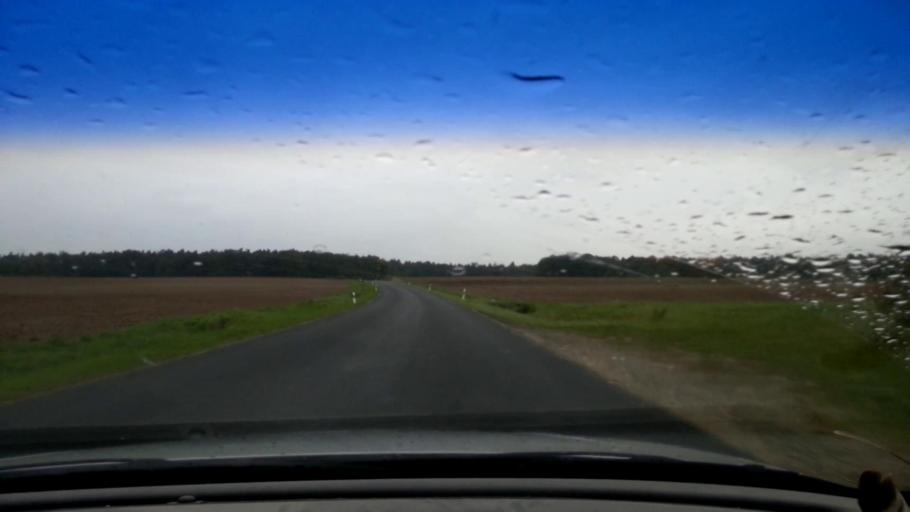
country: DE
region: Bavaria
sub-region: Upper Franconia
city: Priesendorf
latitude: 49.8629
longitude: 10.6895
